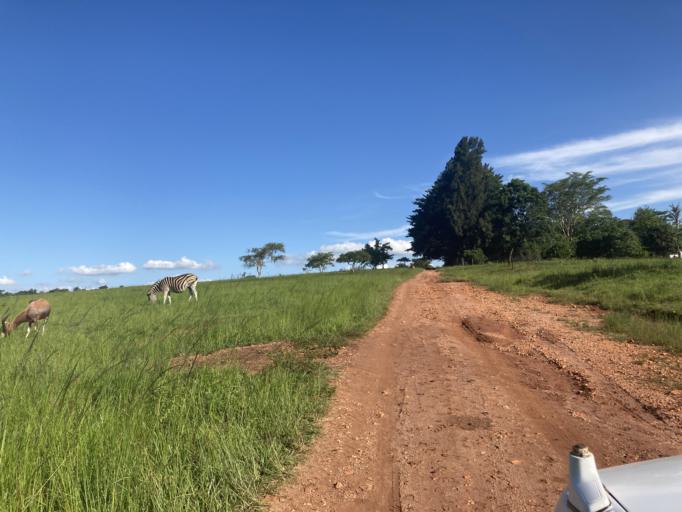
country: SZ
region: Hhohho
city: Lobamba
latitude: -26.4936
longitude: 31.1946
